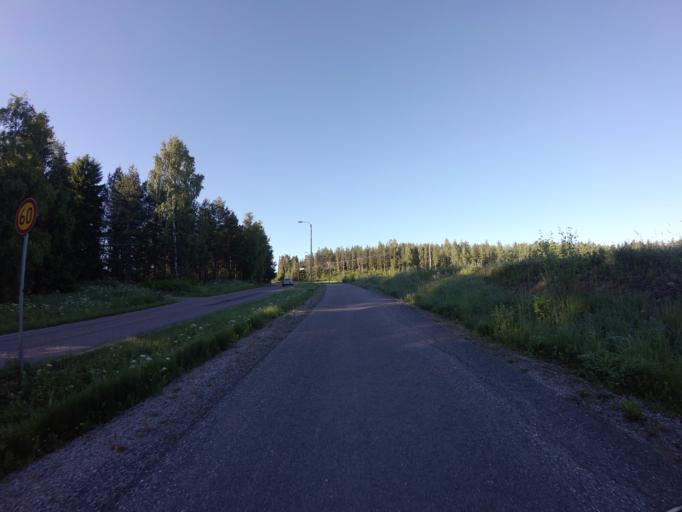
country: FI
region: Varsinais-Suomi
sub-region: Turku
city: Vahto
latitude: 60.5347
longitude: 22.3438
